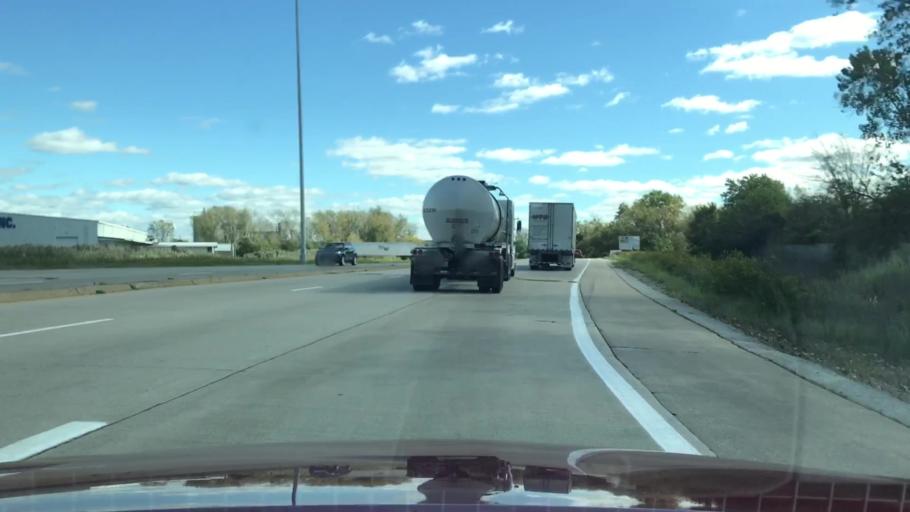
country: US
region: Illinois
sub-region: Cook County
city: Dolton
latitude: 41.6601
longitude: -87.5854
